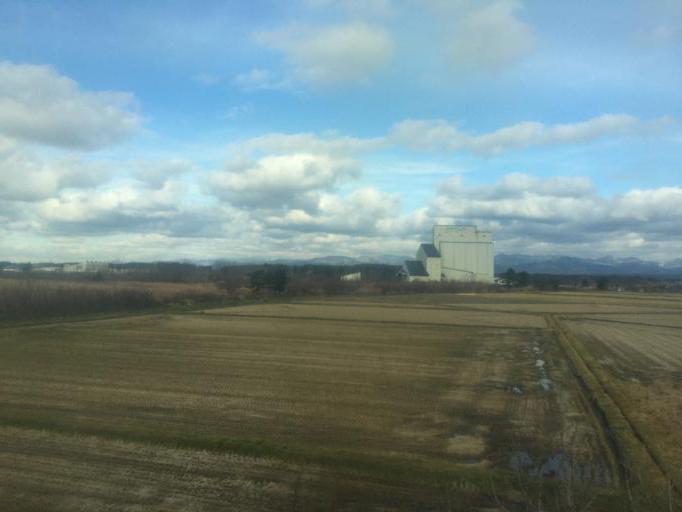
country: JP
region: Akita
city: Noshiromachi
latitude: 40.1951
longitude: 140.0843
